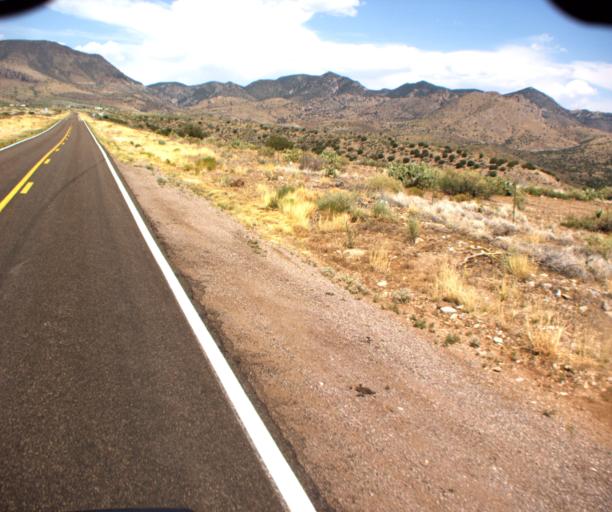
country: US
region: Arizona
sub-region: Greenlee County
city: Clifton
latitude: 33.0295
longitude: -109.1429
